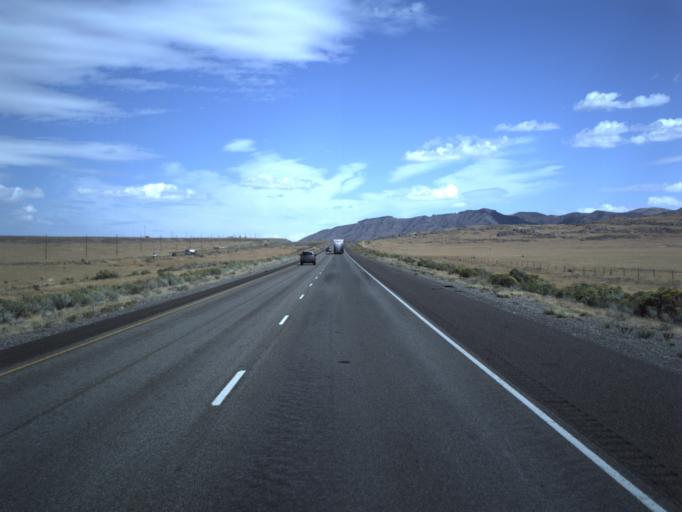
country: US
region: Utah
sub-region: Tooele County
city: Grantsville
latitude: 40.7529
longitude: -113.0358
